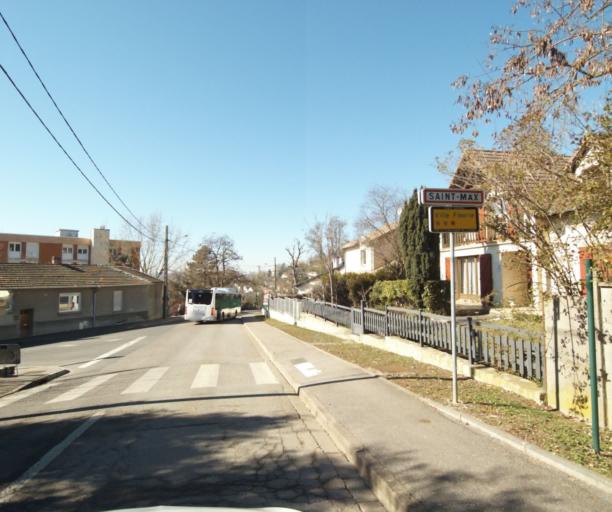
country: FR
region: Lorraine
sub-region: Departement de Meurthe-et-Moselle
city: Saint-Max
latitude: 48.7113
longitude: 6.2071
